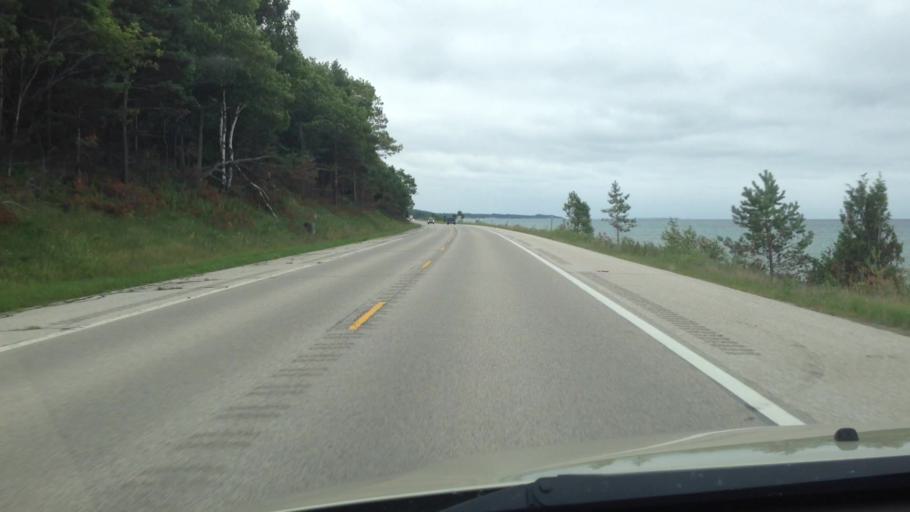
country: US
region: Michigan
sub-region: Mackinac County
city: Saint Ignace
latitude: 45.9980
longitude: -84.9912
